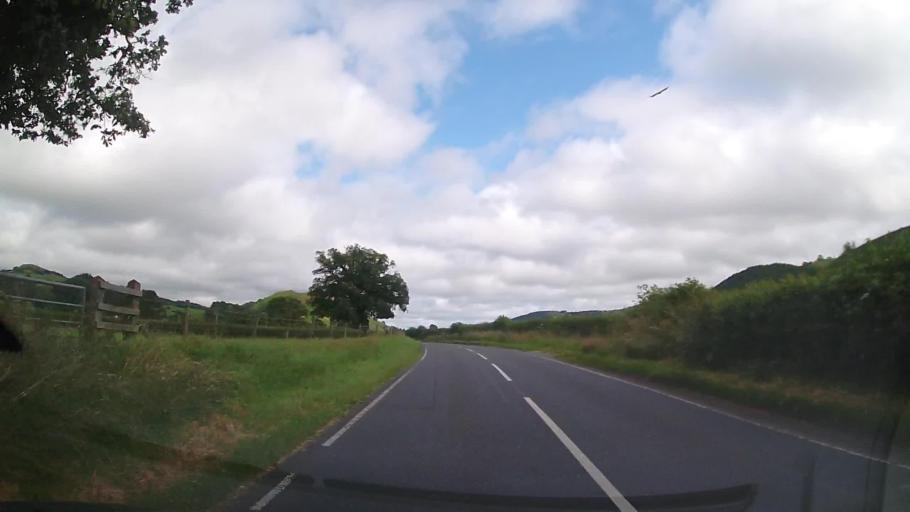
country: GB
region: Wales
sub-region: Sir Powys
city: Llanrhaeadr-ym-Mochnant
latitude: 52.8129
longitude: -3.2598
